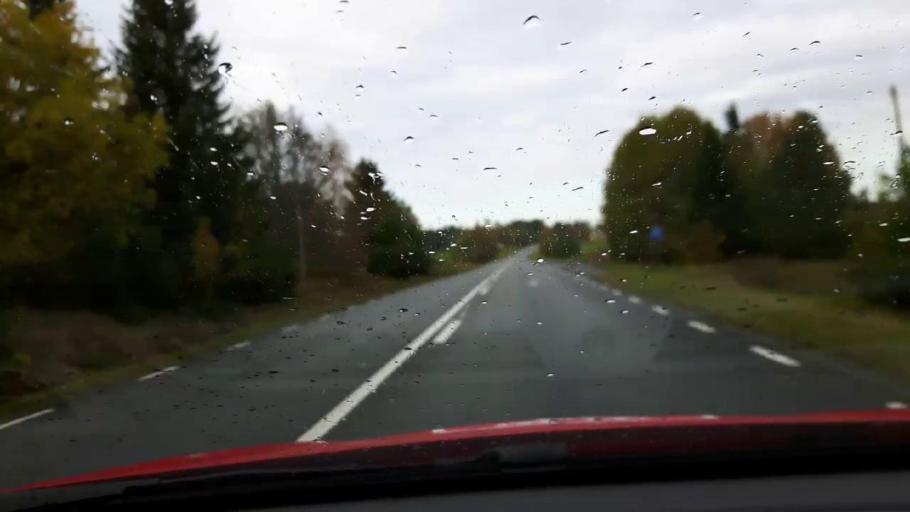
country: SE
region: Jaemtland
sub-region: Krokoms Kommun
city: Krokom
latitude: 63.1011
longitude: 14.2998
